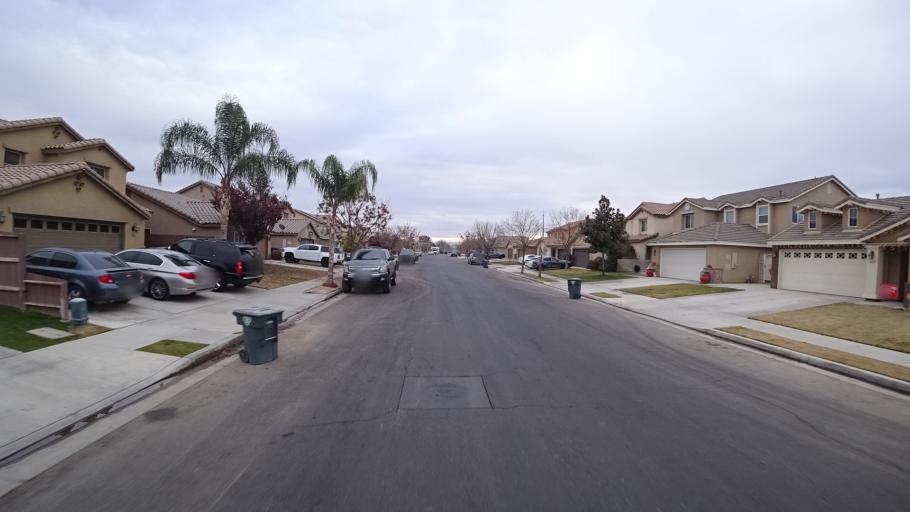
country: US
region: California
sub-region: Kern County
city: Greenfield
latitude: 35.2976
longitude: -119.0720
